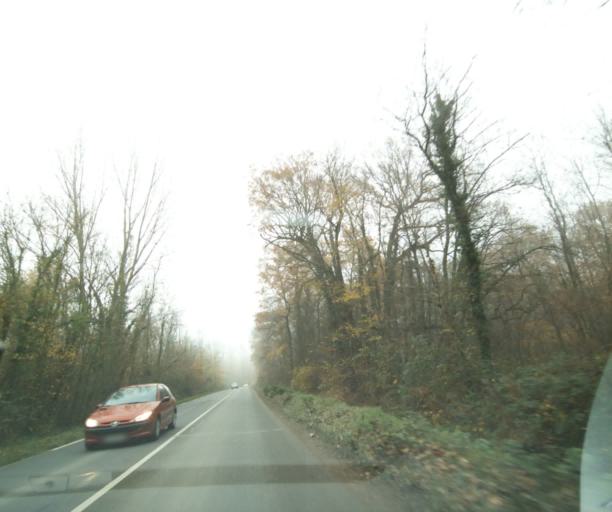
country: FR
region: Ile-de-France
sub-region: Departement de Seine-Saint-Denis
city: Clichy-sous-Bois
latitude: 48.9178
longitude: 2.5559
